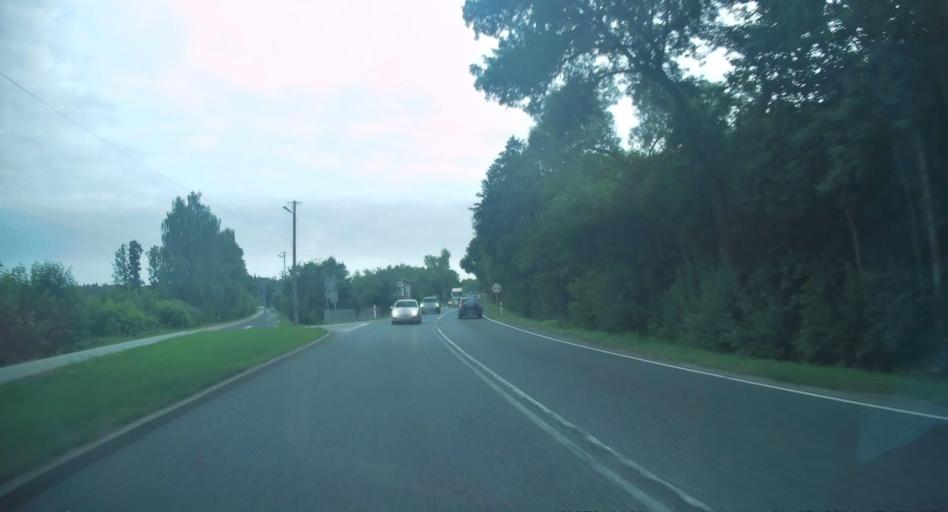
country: PL
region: Lodz Voivodeship
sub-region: Powiat radomszczanski
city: Kamiensk
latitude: 51.1889
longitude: 19.4974
